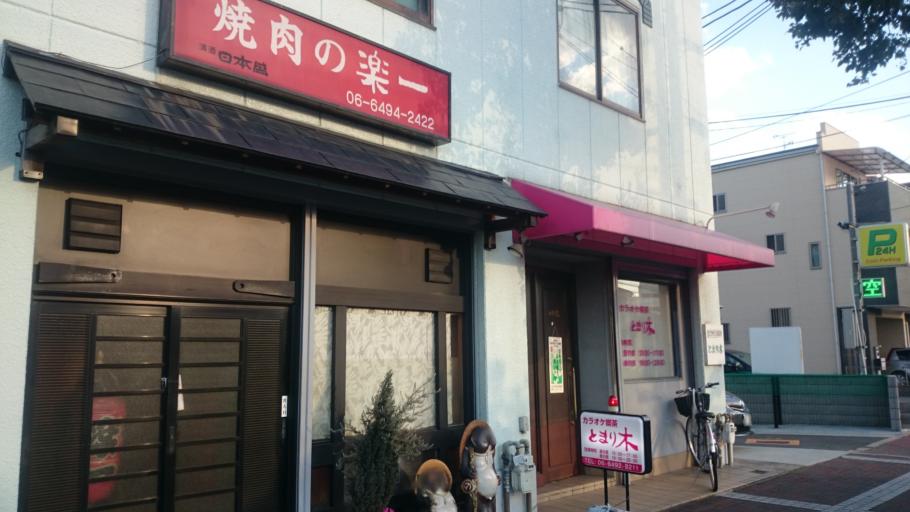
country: JP
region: Osaka
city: Toyonaka
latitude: 34.7554
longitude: 135.4464
